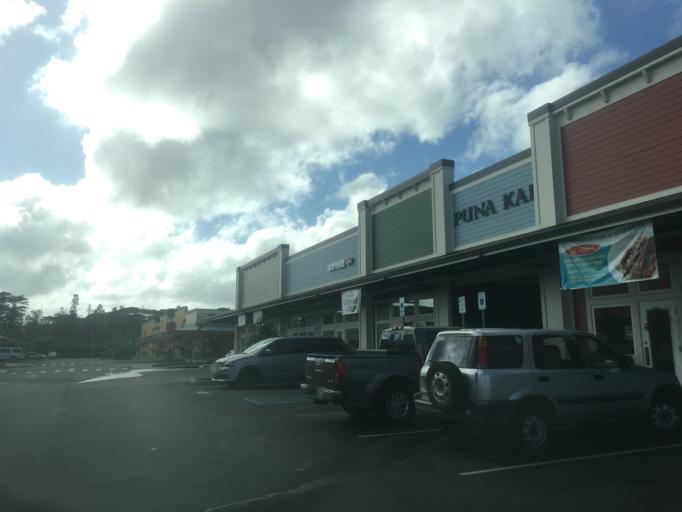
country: US
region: Hawaii
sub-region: Hawaii County
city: Hawaiian Paradise Park
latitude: 19.5031
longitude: -154.9565
